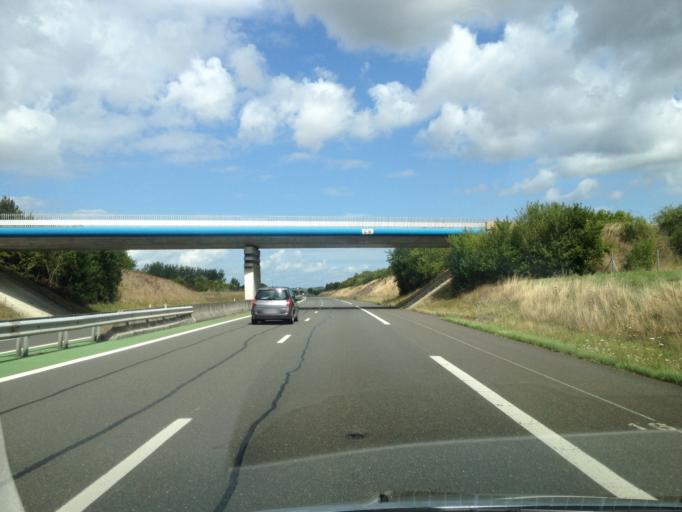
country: FR
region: Pays de la Loire
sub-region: Departement de Maine-et-Loire
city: Saint-Lambert-du-Lattay
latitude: 47.2711
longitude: -0.6142
